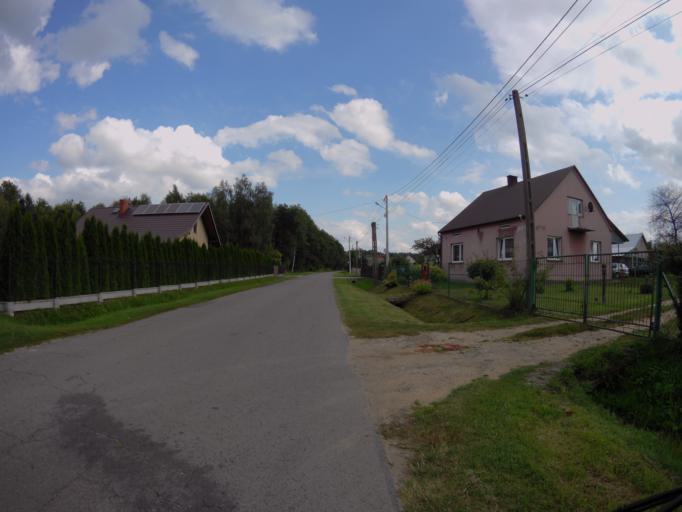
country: PL
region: Subcarpathian Voivodeship
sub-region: Powiat lezajski
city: Brzoza Krolewska
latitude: 50.2435
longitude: 22.3440
